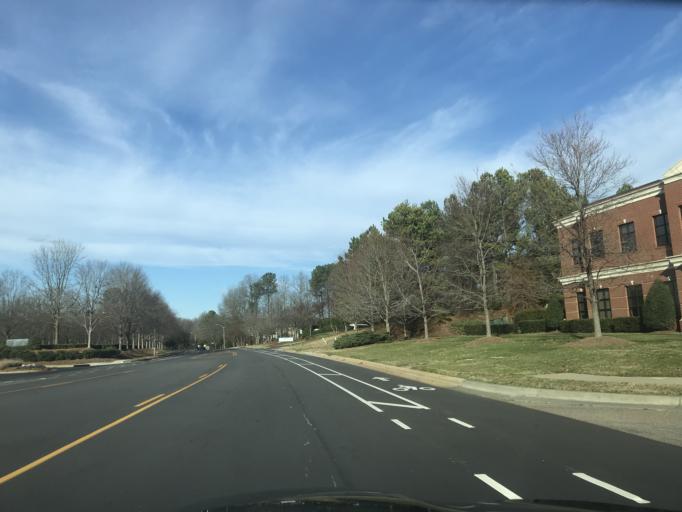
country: US
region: North Carolina
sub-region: Wake County
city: Cary
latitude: 35.7924
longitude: -78.7395
